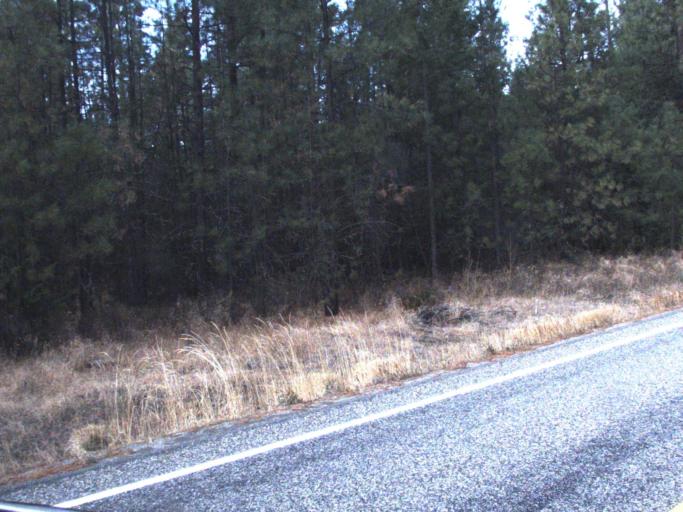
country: US
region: Washington
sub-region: Stevens County
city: Kettle Falls
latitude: 48.7584
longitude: -118.0394
